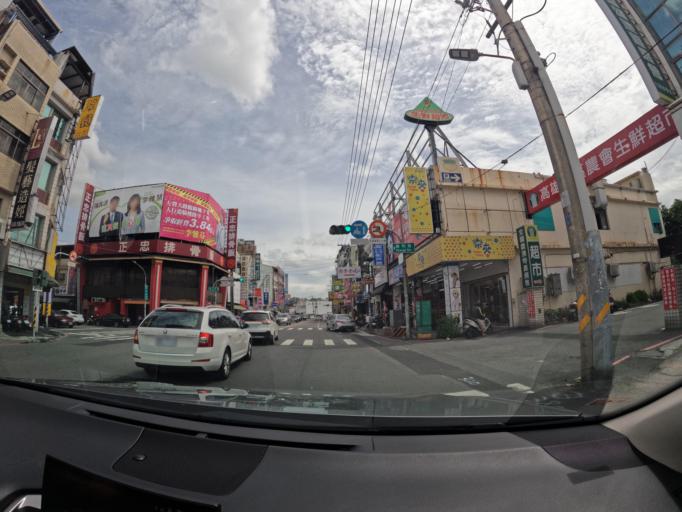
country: TW
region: Kaohsiung
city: Kaohsiung
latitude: 22.6819
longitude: 120.2882
